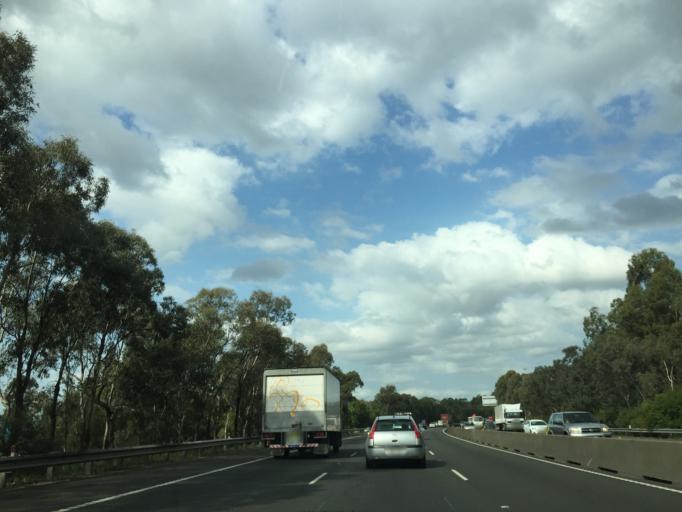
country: AU
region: New South Wales
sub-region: Holroyd
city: Girraween
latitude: -33.8066
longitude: 150.9294
